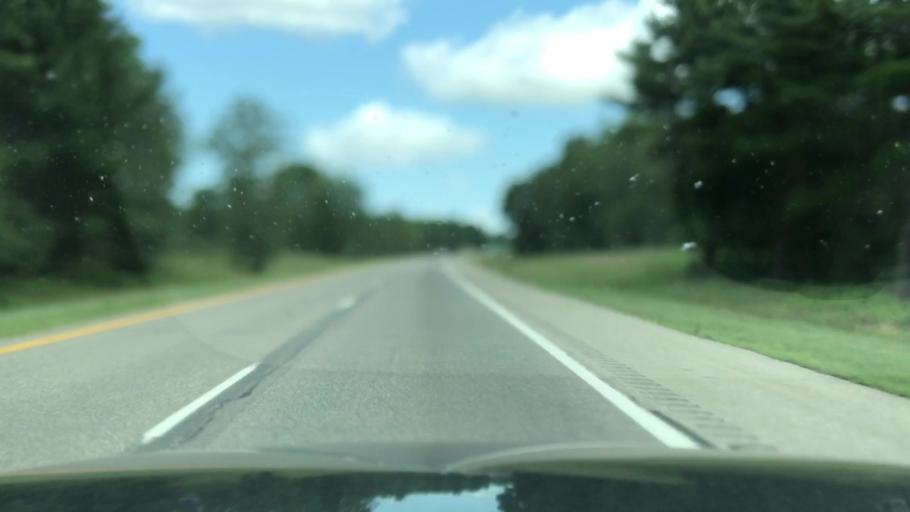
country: US
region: Michigan
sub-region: Mecosta County
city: Big Rapids
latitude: 43.6977
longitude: -85.5261
